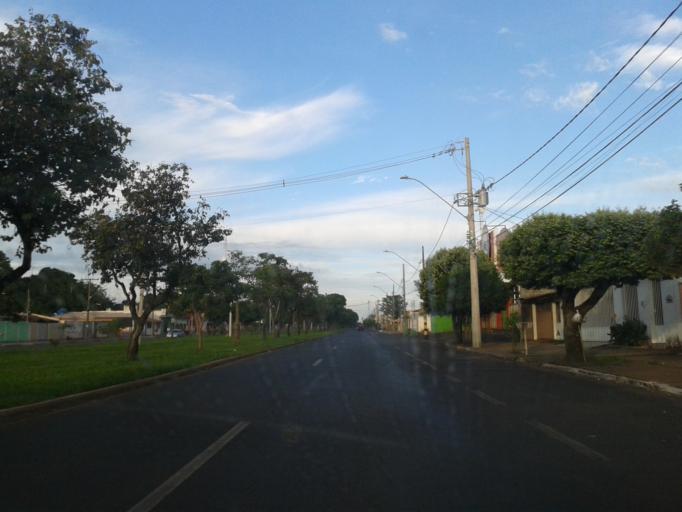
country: BR
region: Minas Gerais
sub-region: Araguari
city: Araguari
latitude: -18.6407
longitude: -48.1963
